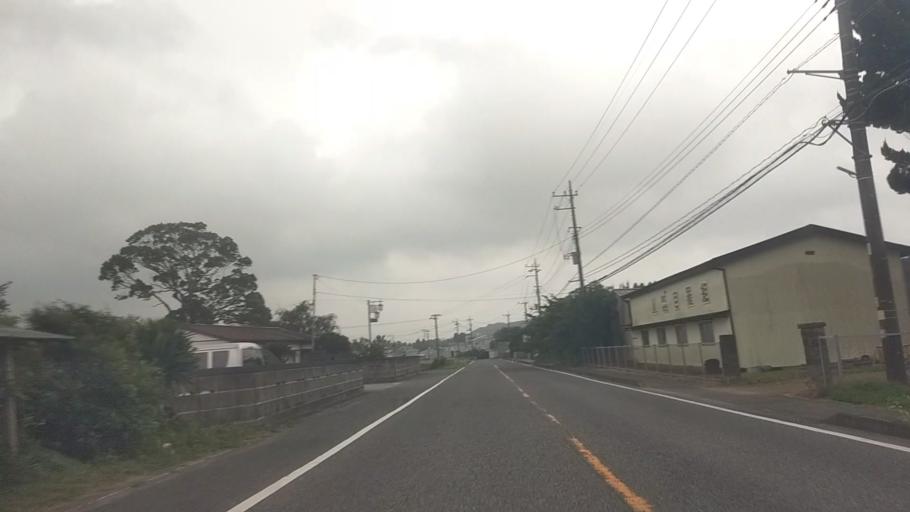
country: JP
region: Chiba
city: Ohara
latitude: 35.2814
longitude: 140.2958
